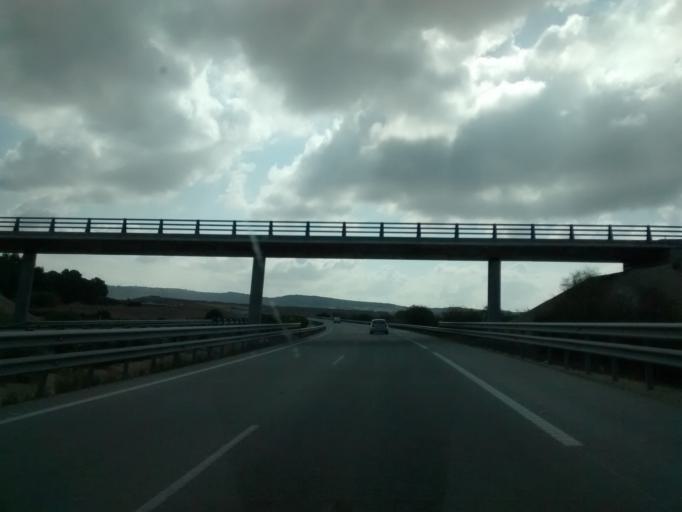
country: ES
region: Andalusia
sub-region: Provincia de Cadiz
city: Vejer de la Frontera
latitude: 36.2499
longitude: -6.0215
